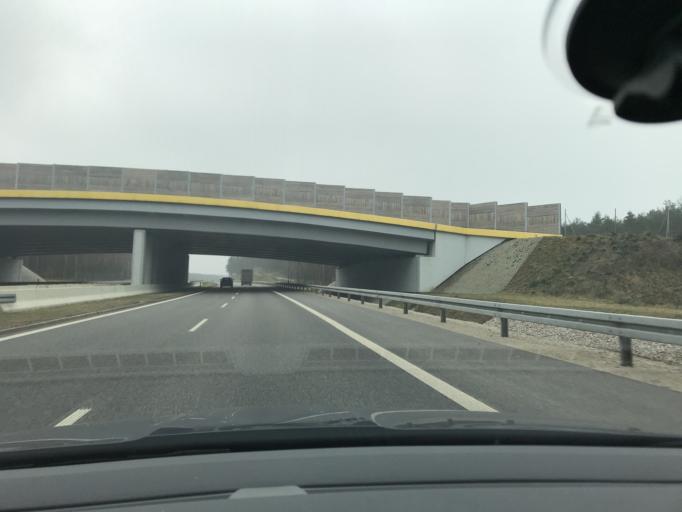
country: PL
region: Lodz Voivodeship
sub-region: Powiat pabianicki
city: Dobron
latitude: 51.6291
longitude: 19.2709
